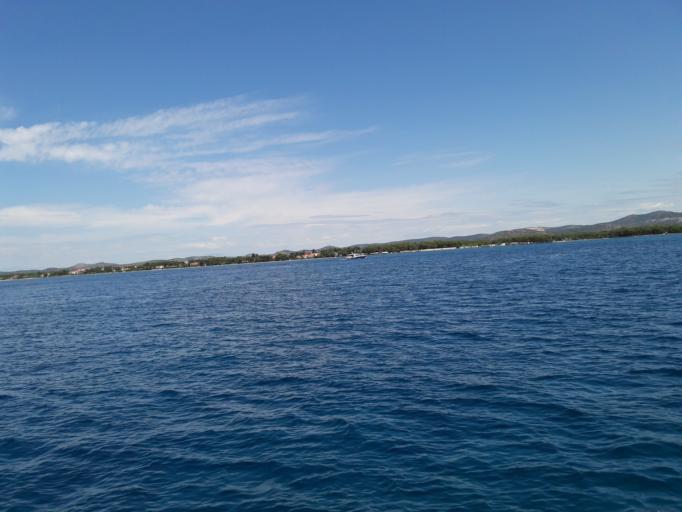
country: HR
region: Sibensko-Kniniska
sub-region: Grad Sibenik
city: Sibenik
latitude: 43.7156
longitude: 15.8412
